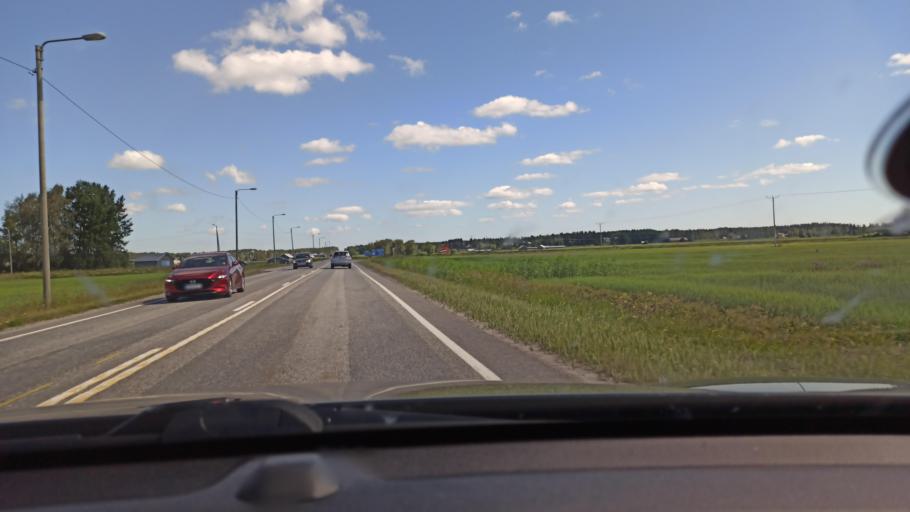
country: FI
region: Ostrobothnia
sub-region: Vaasa
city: Teeriniemi
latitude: 63.0030
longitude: 21.6775
